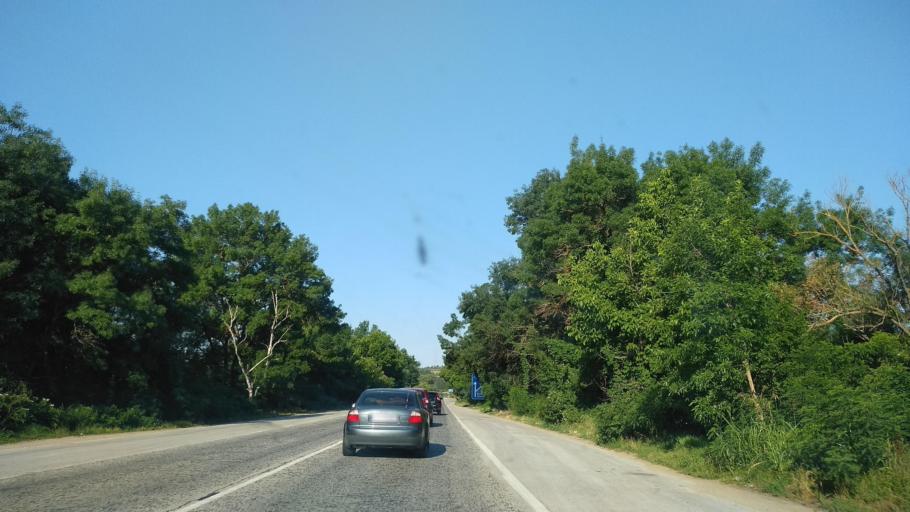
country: BG
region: Lovech
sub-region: Obshtina Lovech
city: Lovech
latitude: 43.0475
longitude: 24.8873
